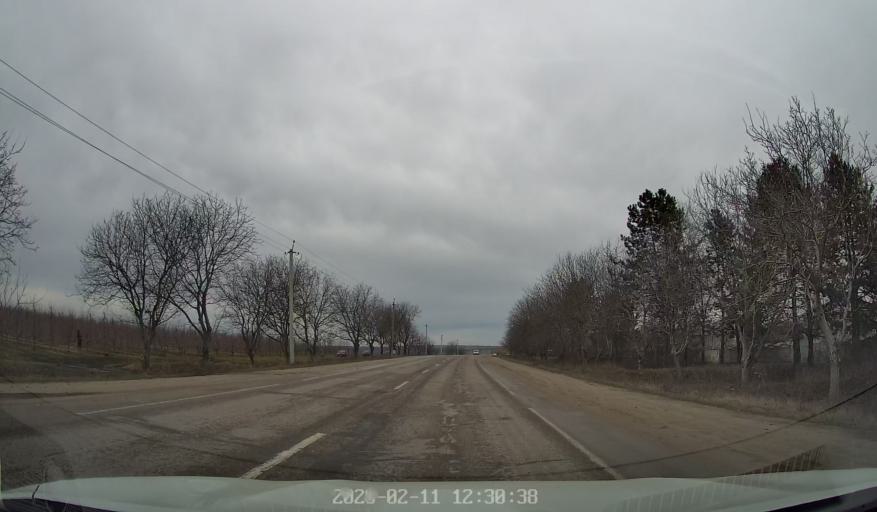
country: MD
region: Raionul Edinet
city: Edinet
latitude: 48.1662
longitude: 27.2814
